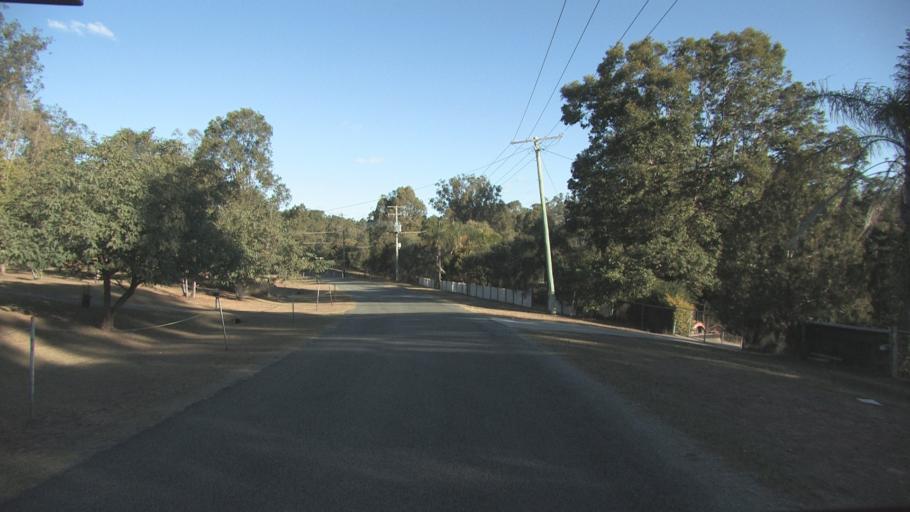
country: AU
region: Queensland
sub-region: Logan
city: Cedar Vale
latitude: -27.8558
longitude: 152.9810
